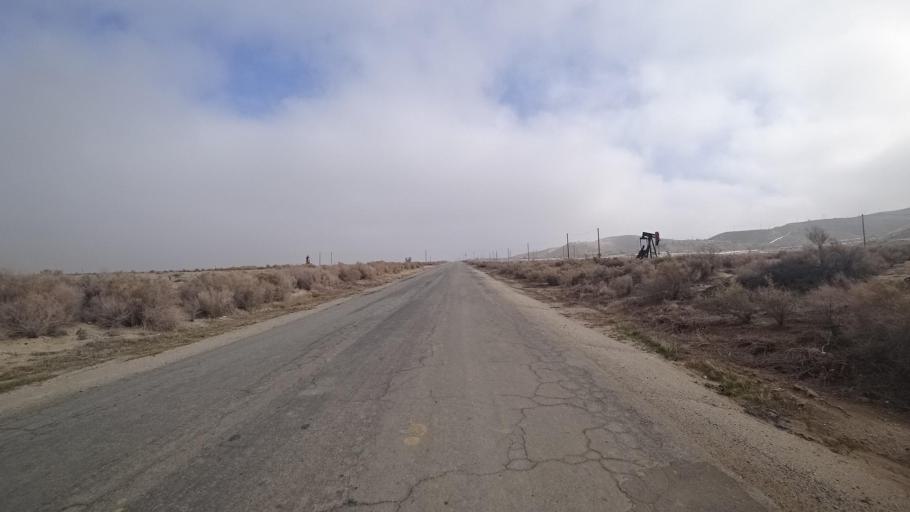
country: US
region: California
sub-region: Kern County
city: Maricopa
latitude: 35.0383
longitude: -119.3732
